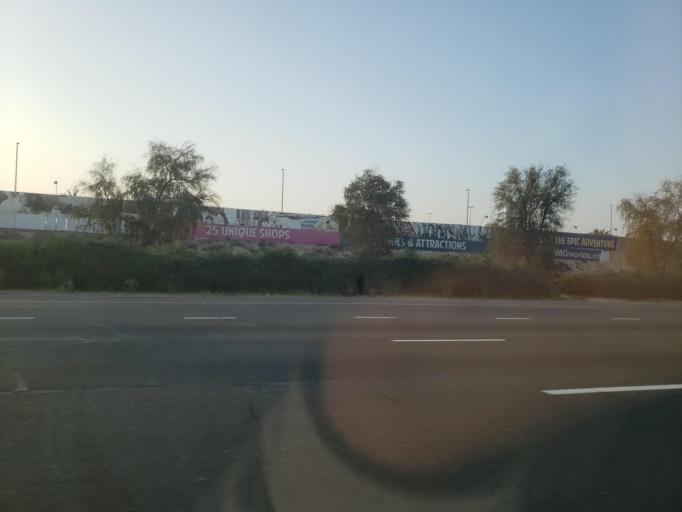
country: AE
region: Dubai
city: Dubai
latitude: 25.0922
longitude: 55.3269
